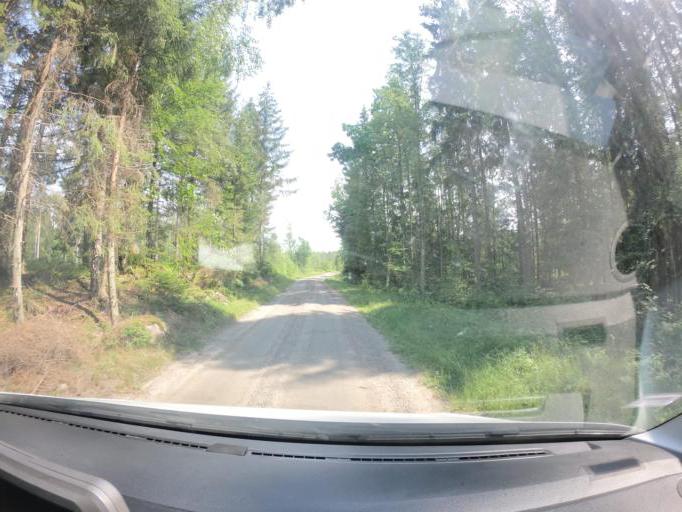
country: SE
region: Kronoberg
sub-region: Markaryds Kommun
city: Markaryd
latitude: 56.3876
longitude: 13.5427
